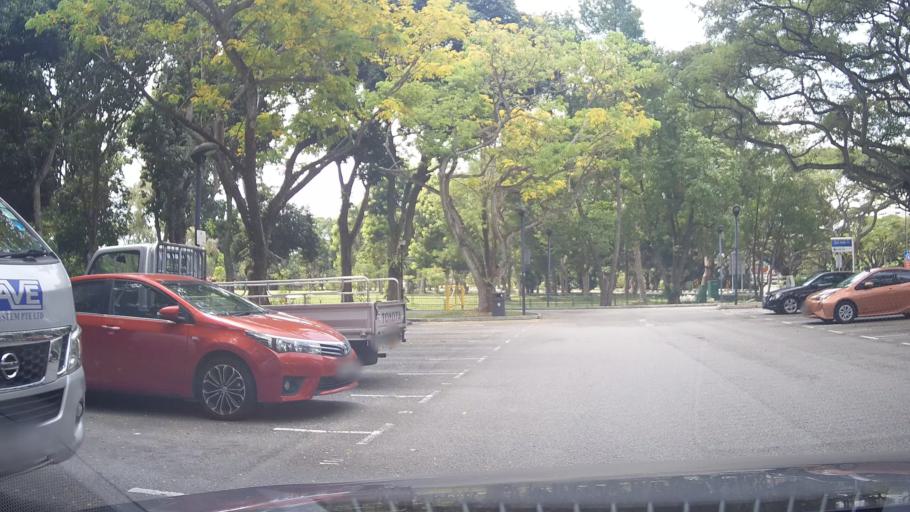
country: SG
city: Singapore
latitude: 1.3095
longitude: 103.9383
